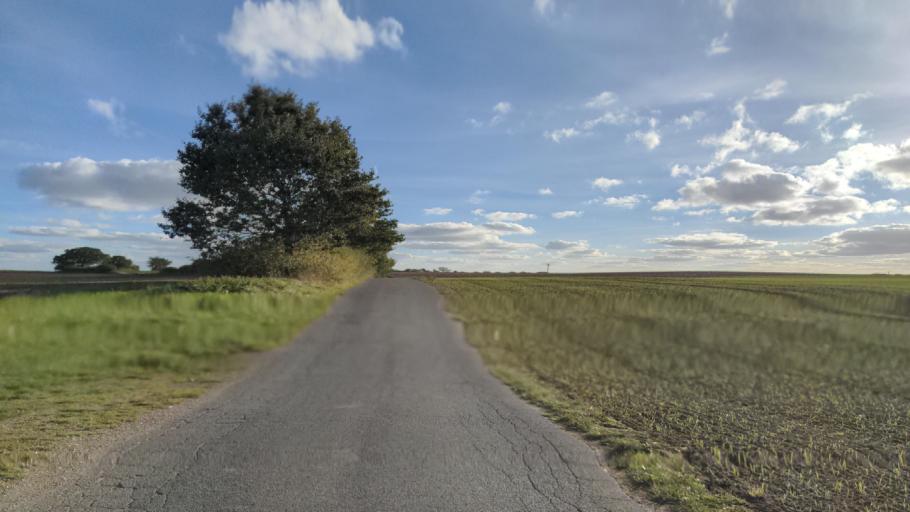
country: DE
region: Schleswig-Holstein
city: Schashagen
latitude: 54.1412
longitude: 10.9031
